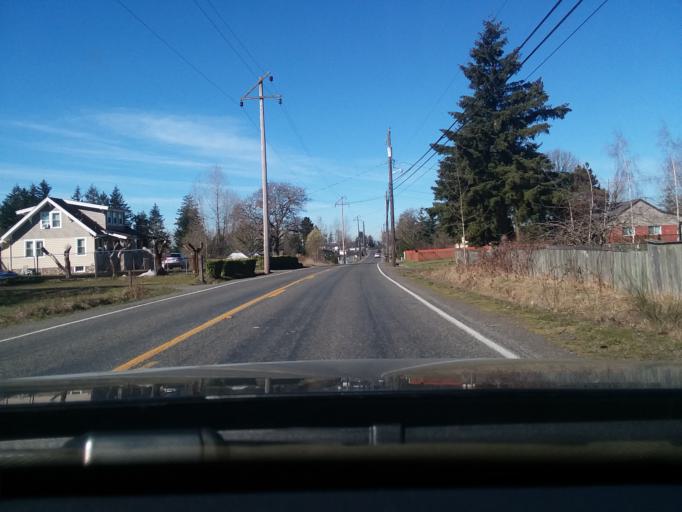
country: US
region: Washington
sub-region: Pierce County
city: Midland
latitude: 47.1622
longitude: -122.4004
